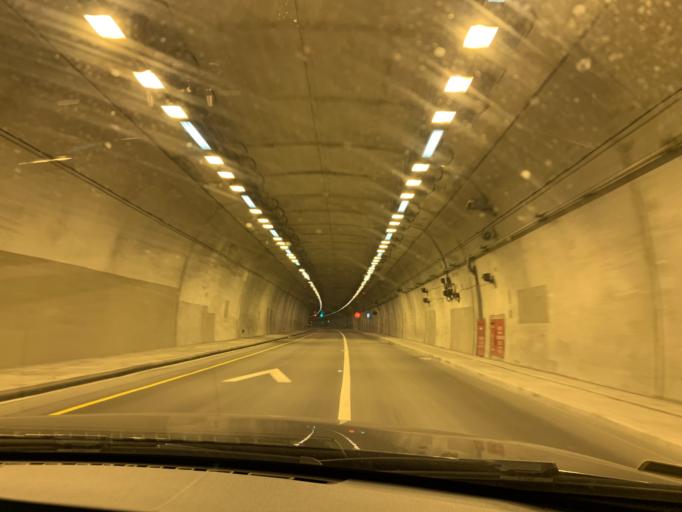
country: TW
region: Taiwan
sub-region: Yilan
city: Yilan
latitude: 24.5342
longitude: 121.8357
